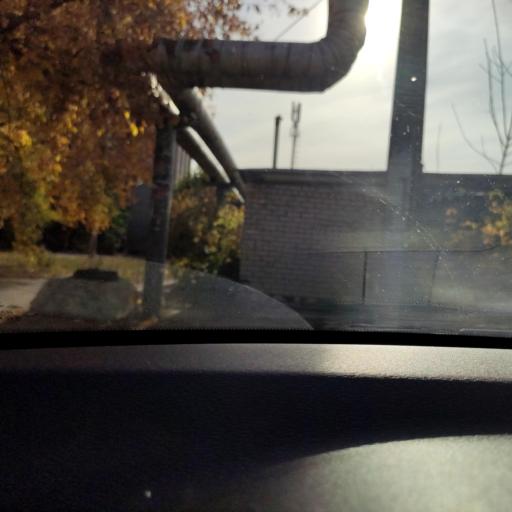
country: RU
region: Samara
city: Samara
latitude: 53.2349
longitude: 50.2061
